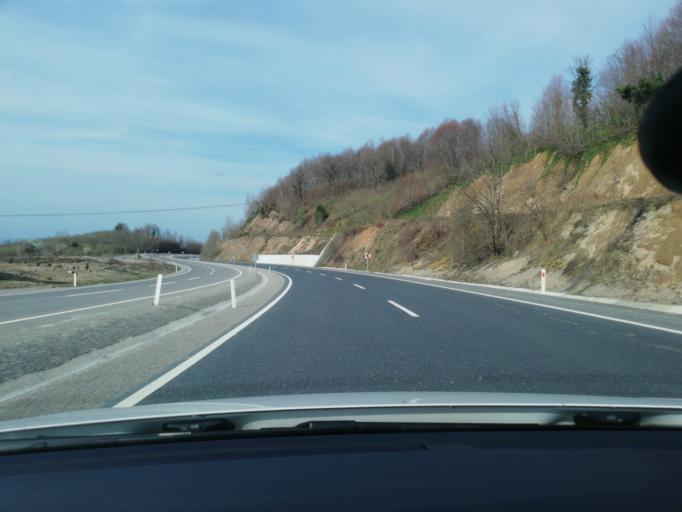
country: TR
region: Zonguldak
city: Kozlu
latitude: 41.3381
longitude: 31.6290
